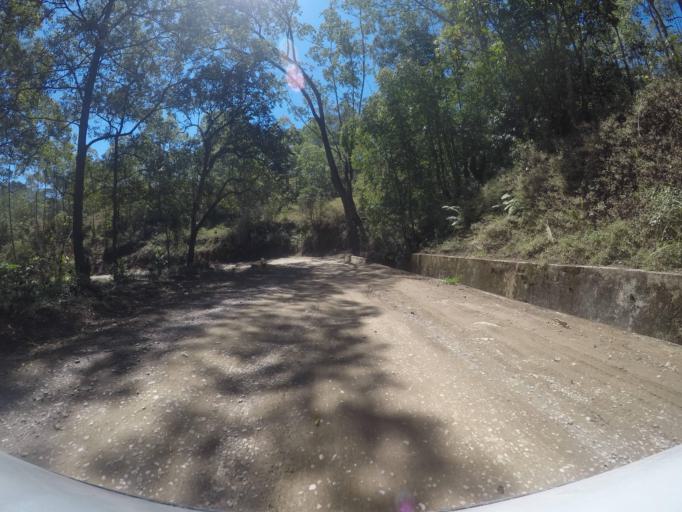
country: TL
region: Ermera
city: Gleno
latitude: -8.7816
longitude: 125.3797
